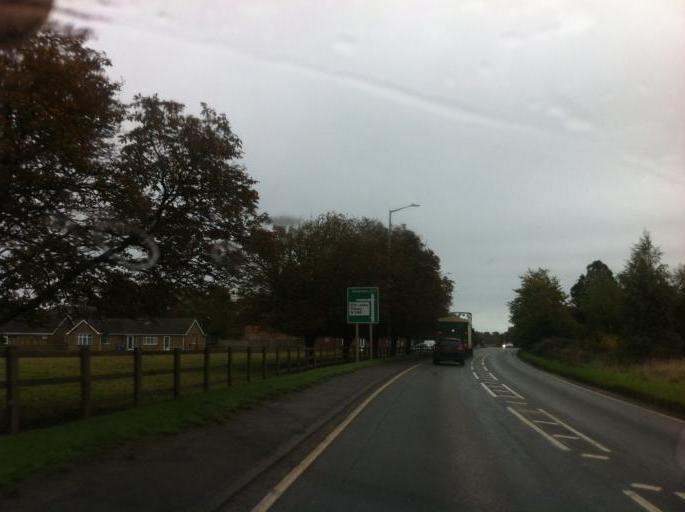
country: GB
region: England
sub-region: Lincolnshire
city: Boston
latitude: 53.0278
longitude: 0.0975
